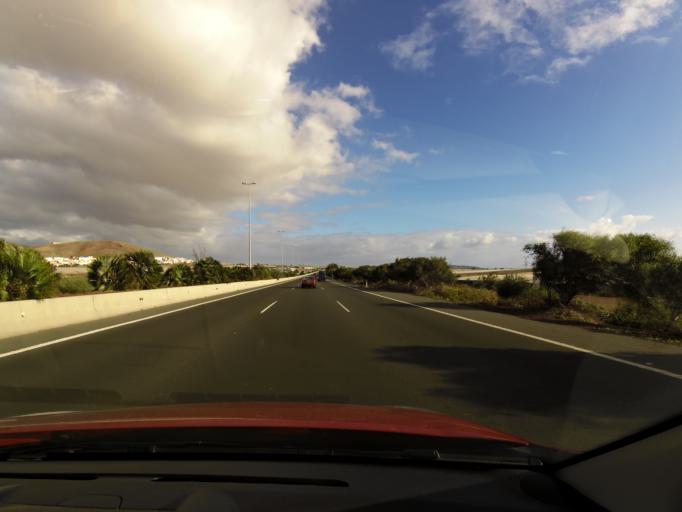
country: ES
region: Canary Islands
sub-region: Provincia de Las Palmas
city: Cruce de Arinaga
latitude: 27.8903
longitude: -15.4082
